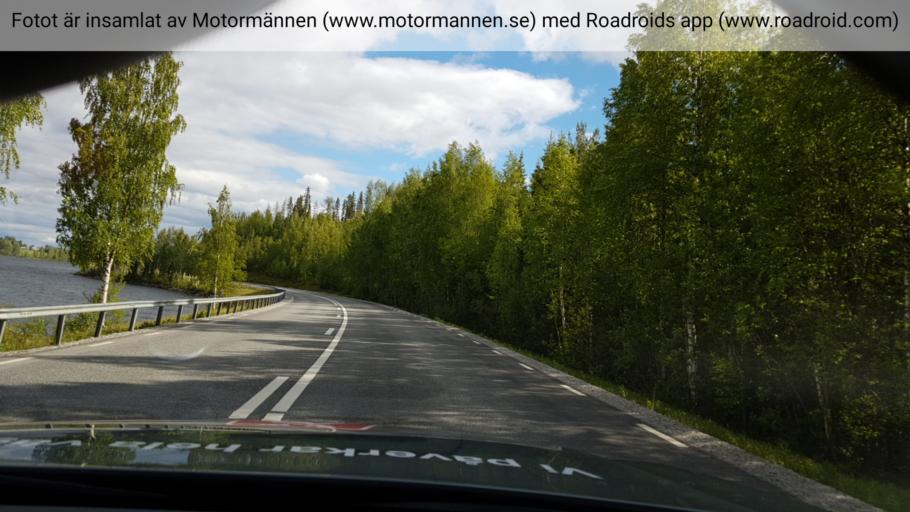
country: SE
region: Jaemtland
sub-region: Stroemsunds Kommun
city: Stroemsund
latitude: 64.1740
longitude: 15.6619
